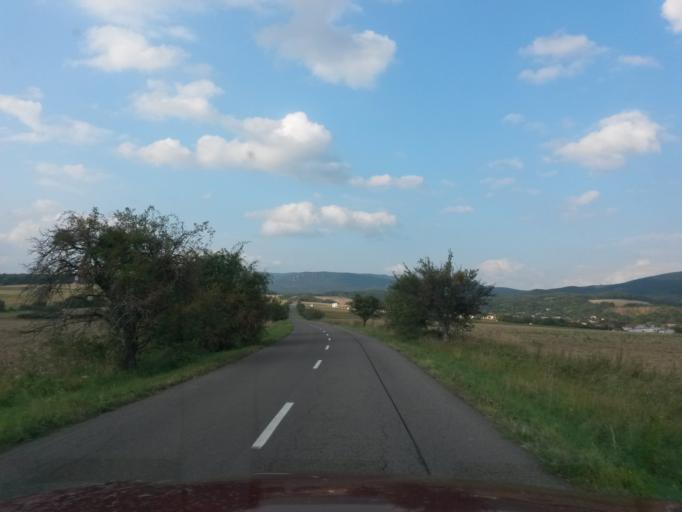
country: SK
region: Kosicky
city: Secovce
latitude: 48.7721
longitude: 21.4746
